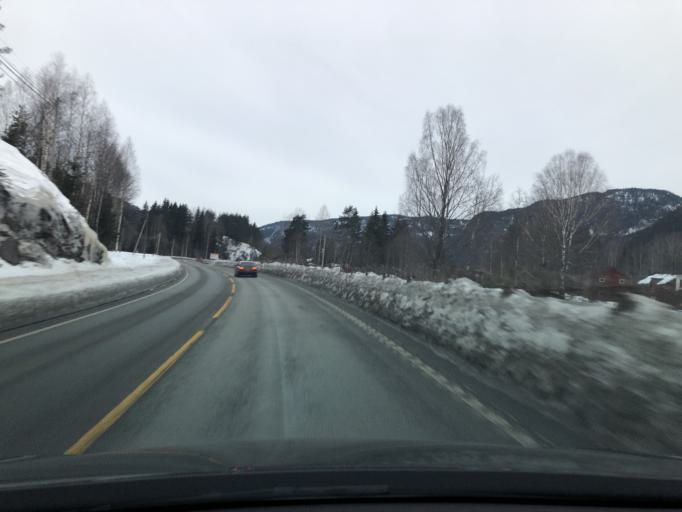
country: NO
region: Oppland
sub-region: Nordre Land
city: Dokka
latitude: 60.6476
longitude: 9.8585
